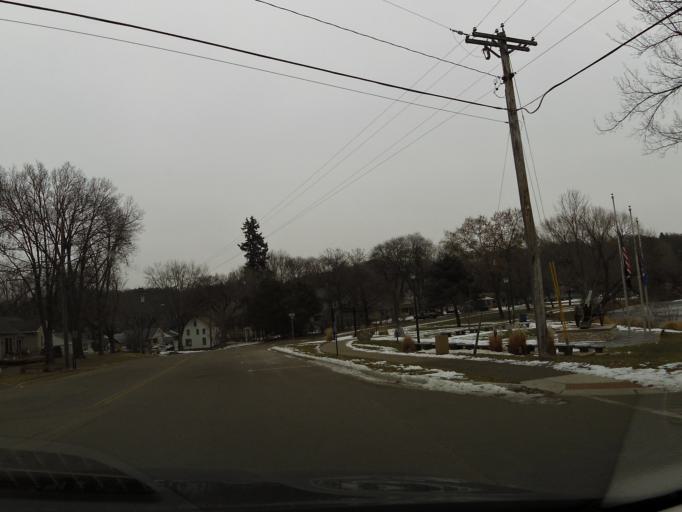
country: US
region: Minnesota
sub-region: Scott County
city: Jordan
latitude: 44.6649
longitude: -93.6307
